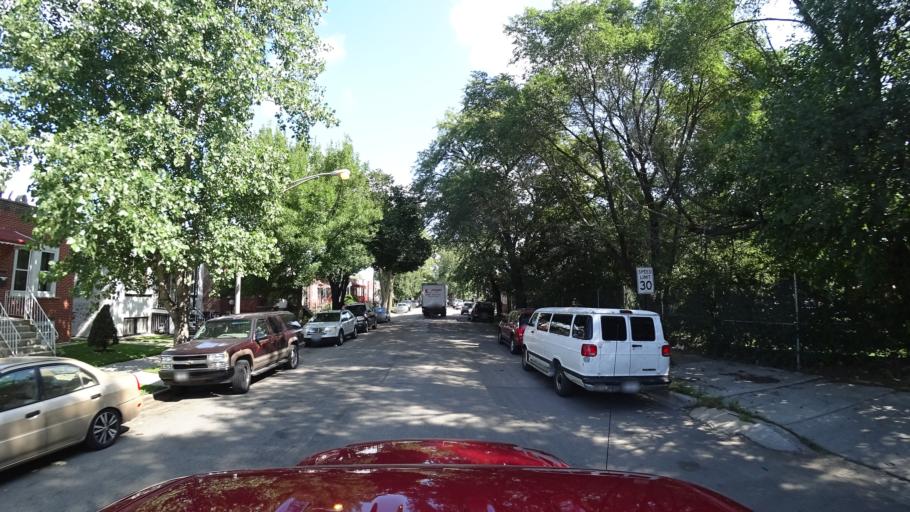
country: US
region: Illinois
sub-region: Cook County
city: Cicero
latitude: 41.8339
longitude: -87.7169
